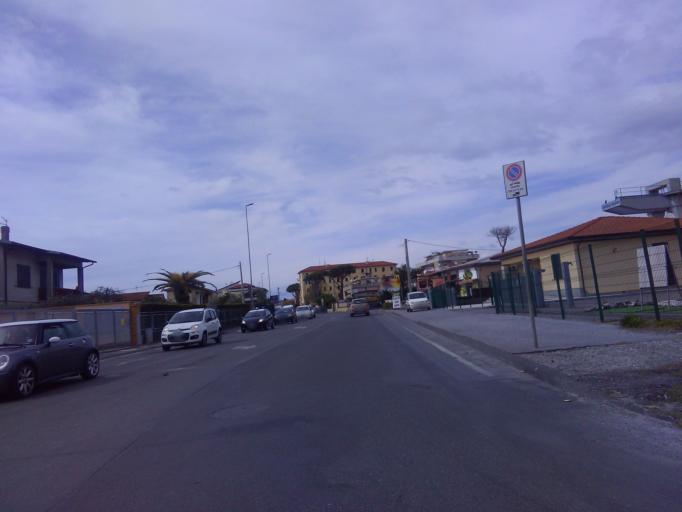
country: IT
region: Tuscany
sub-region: Provincia di Massa-Carrara
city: Carrara
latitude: 44.0432
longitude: 10.0640
